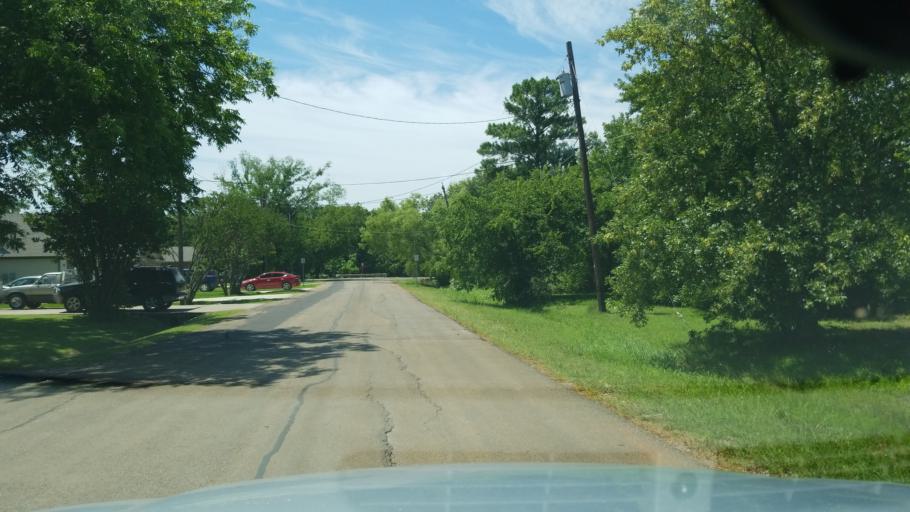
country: US
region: Texas
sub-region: Dallas County
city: Irving
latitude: 32.8161
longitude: -96.9321
